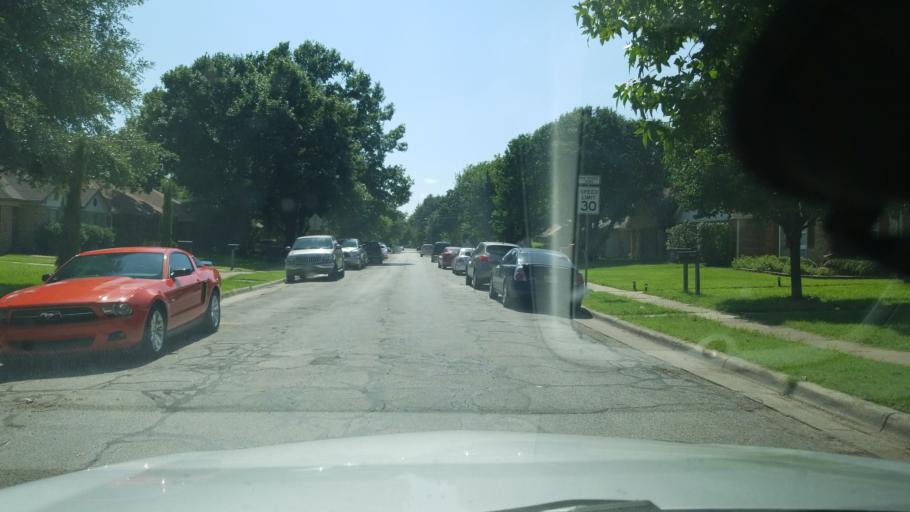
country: US
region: Texas
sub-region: Dallas County
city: Irving
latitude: 32.8128
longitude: -96.9638
